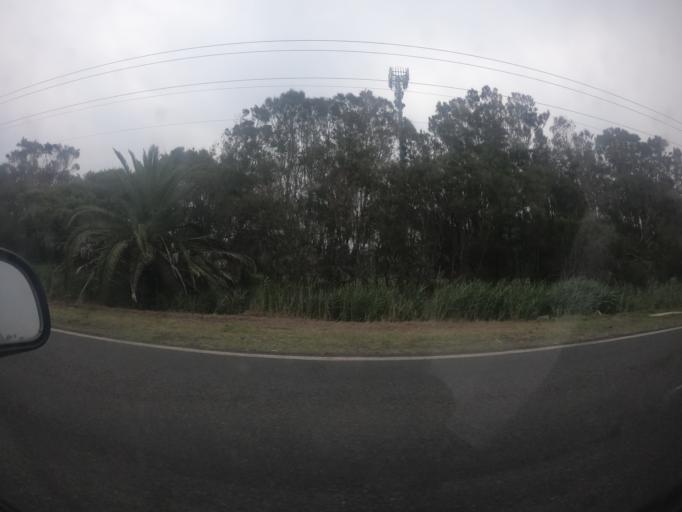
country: AU
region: New South Wales
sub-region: Shellharbour
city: Barrack Heights
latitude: -34.5687
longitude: 150.8665
